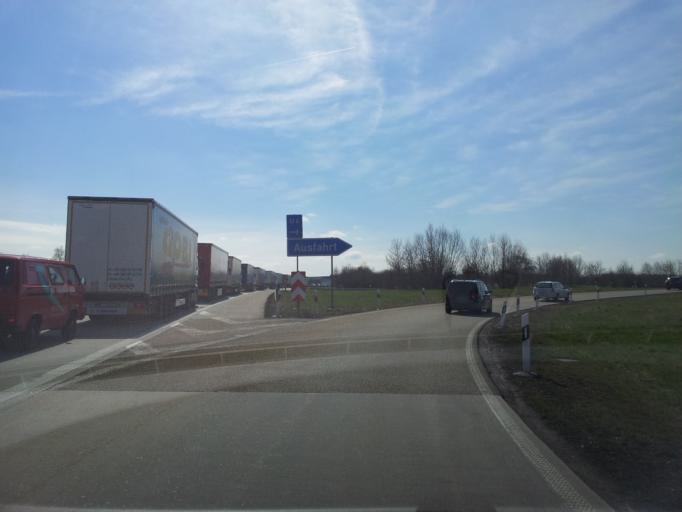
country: DE
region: Saxony
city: Niederdorf
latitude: 50.7299
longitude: 12.7792
